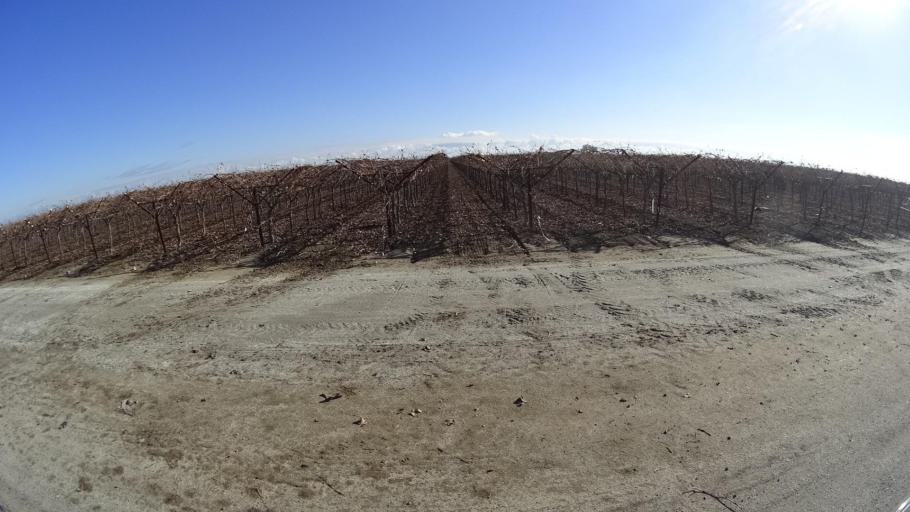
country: US
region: California
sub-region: Kern County
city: Delano
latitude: 35.7199
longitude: -119.2853
